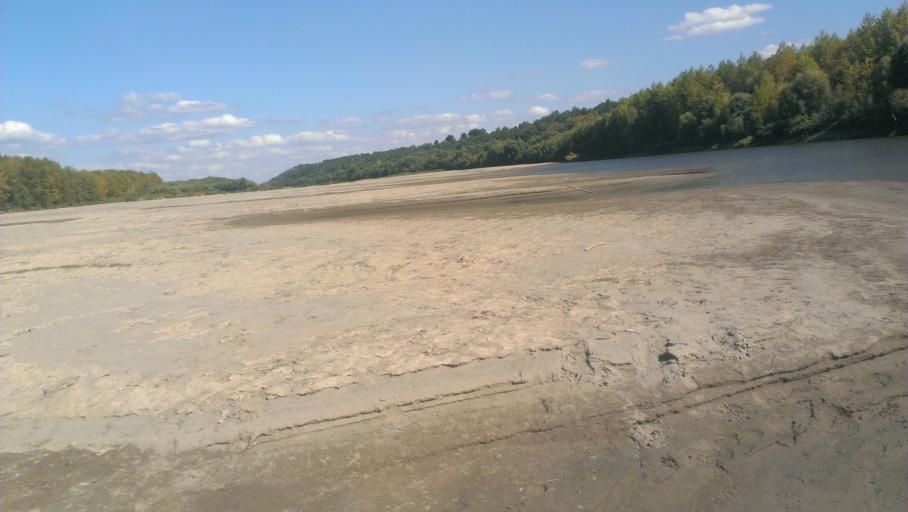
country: RU
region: Altai Krai
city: Nauchnyy Gorodok
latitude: 53.4305
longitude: 83.5096
